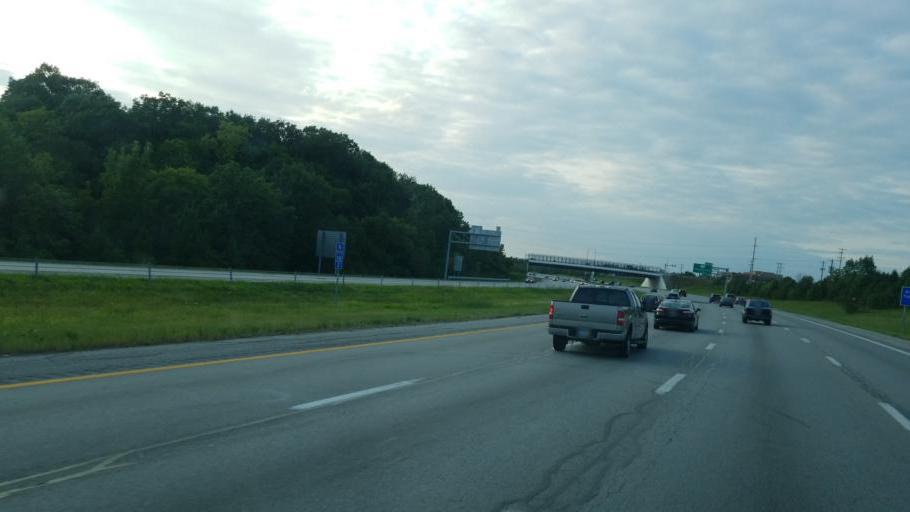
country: US
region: Ohio
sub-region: Franklin County
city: Gahanna
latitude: 39.9962
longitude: -82.8565
